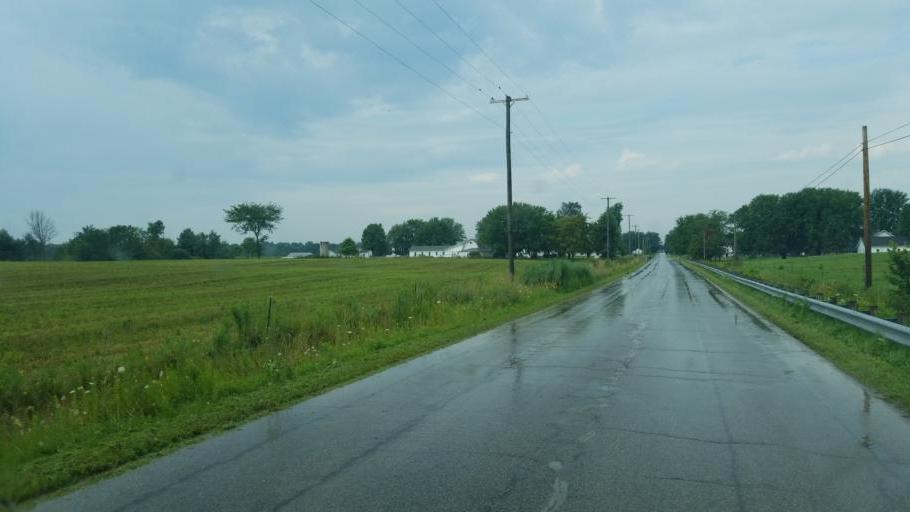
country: US
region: Ohio
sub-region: Geauga County
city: Middlefield
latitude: 41.4791
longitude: -81.0290
